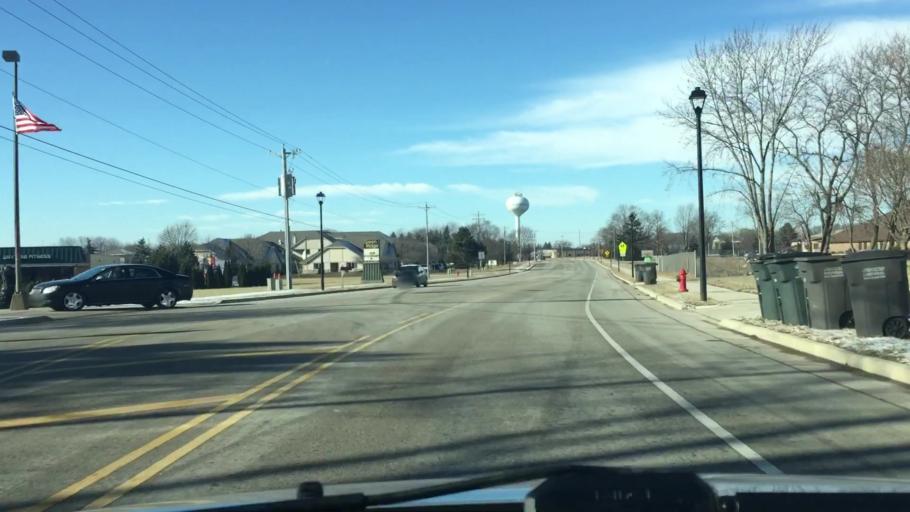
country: US
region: Wisconsin
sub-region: Waukesha County
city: Mukwonago
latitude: 42.8724
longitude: -88.3186
